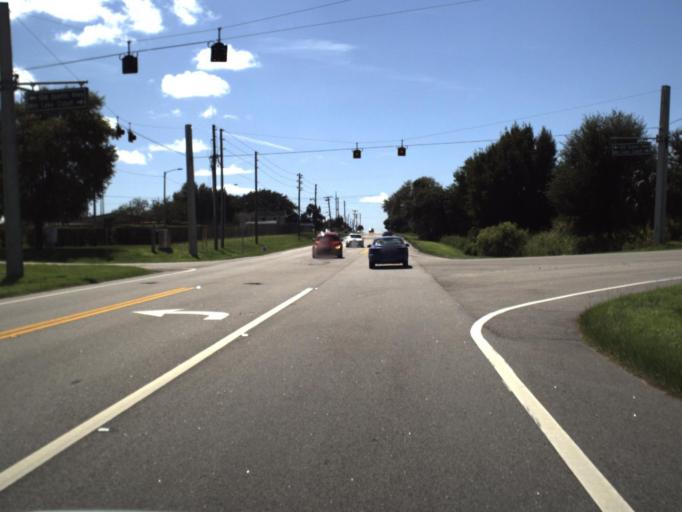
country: US
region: Florida
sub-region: Polk County
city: Lake Wales
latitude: 27.9249
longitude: -81.5956
